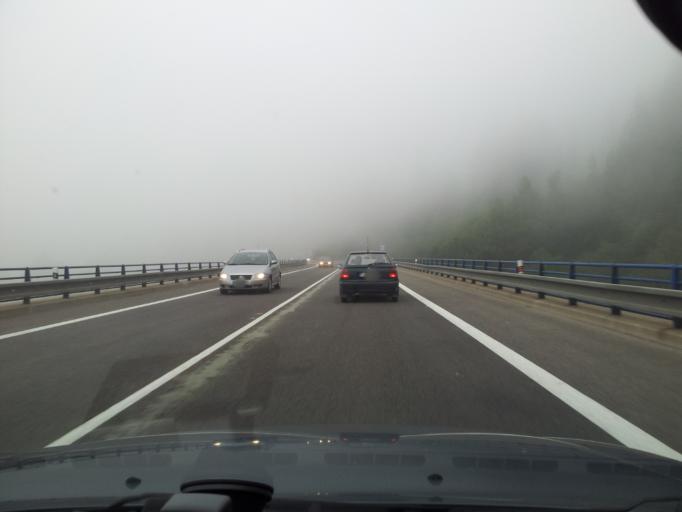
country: SK
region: Zilinsky
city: Cadca
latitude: 49.4293
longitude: 18.8143
